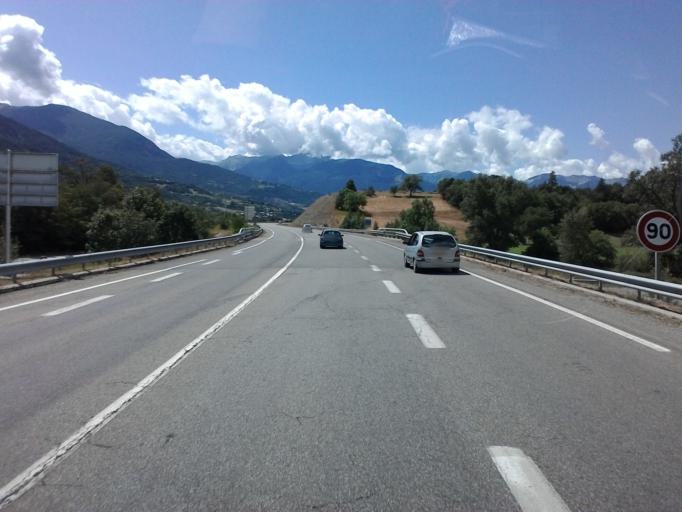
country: FR
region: Provence-Alpes-Cote d'Azur
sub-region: Departement des Hautes-Alpes
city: Embrun
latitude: 44.6094
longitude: 6.5291
